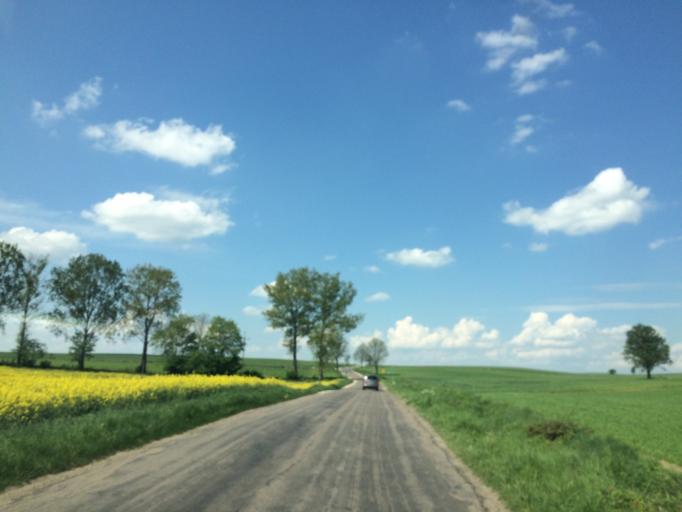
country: PL
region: Warmian-Masurian Voivodeship
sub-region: Powiat dzialdowski
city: Rybno
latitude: 53.3970
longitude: 19.8786
